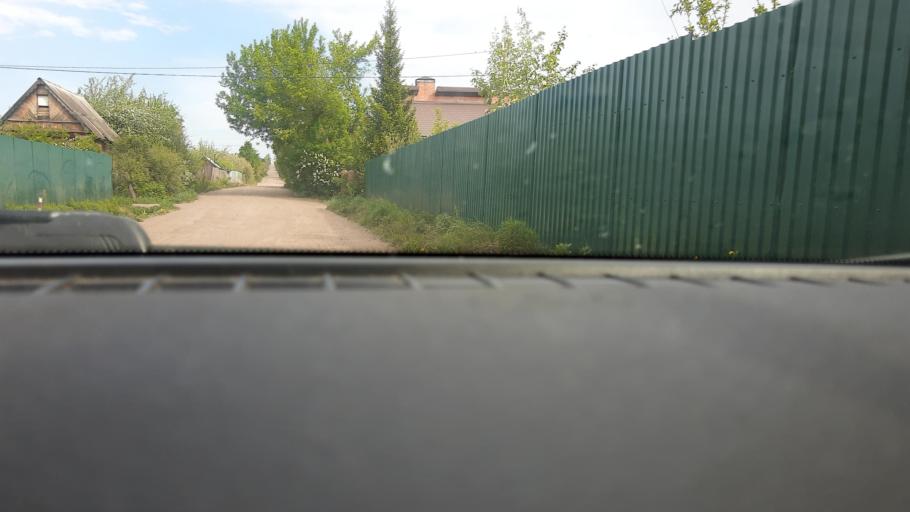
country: RU
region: Bashkortostan
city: Avdon
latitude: 54.5689
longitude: 55.7413
